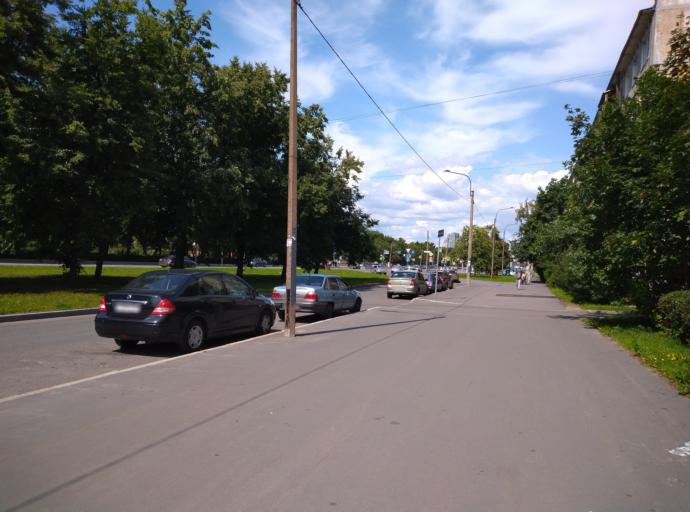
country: RU
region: St.-Petersburg
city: Kupchino
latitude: 59.8629
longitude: 30.3378
